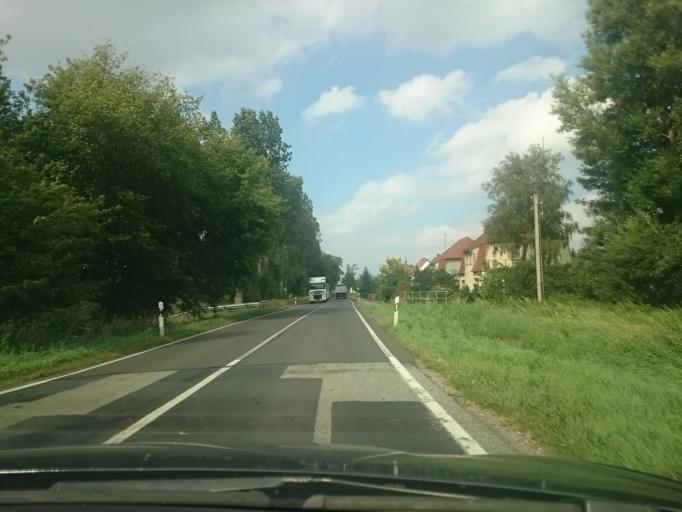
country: DE
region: Mecklenburg-Vorpommern
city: Ducherow
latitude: 53.7568
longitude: 13.7768
